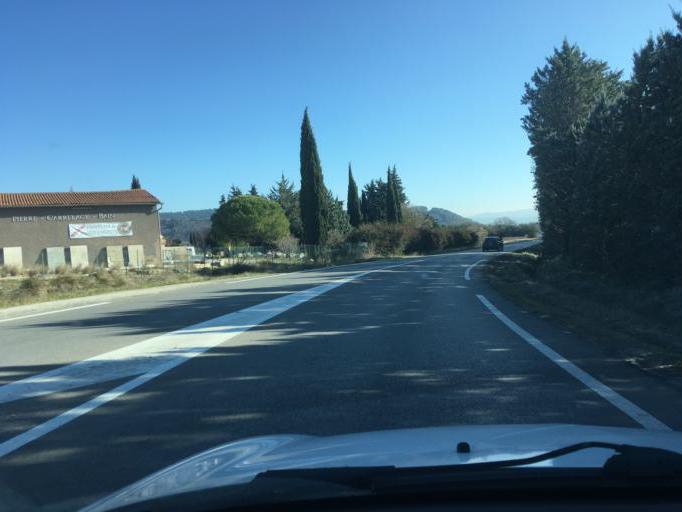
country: FR
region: Provence-Alpes-Cote d'Azur
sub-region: Departement du Vaucluse
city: Lauris
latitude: 43.7514
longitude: 5.3312
